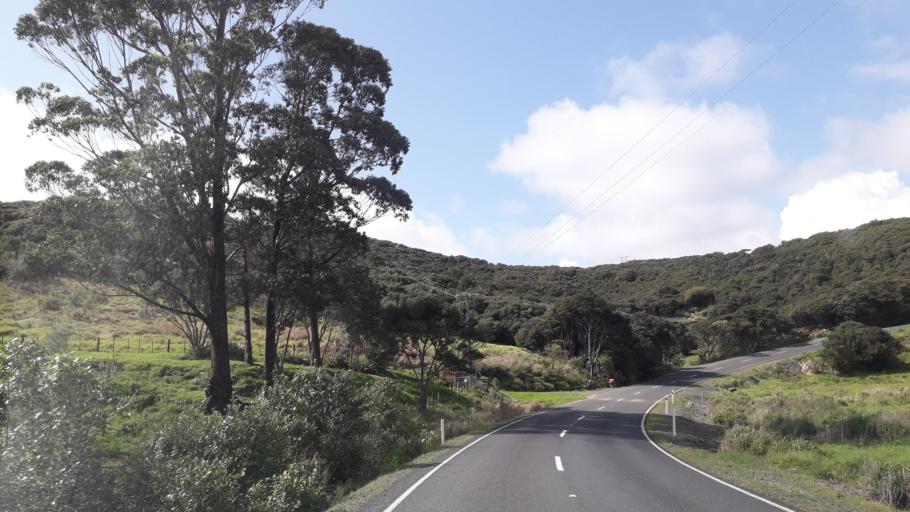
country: NZ
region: Northland
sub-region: Far North District
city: Paihia
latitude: -35.2448
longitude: 174.2548
